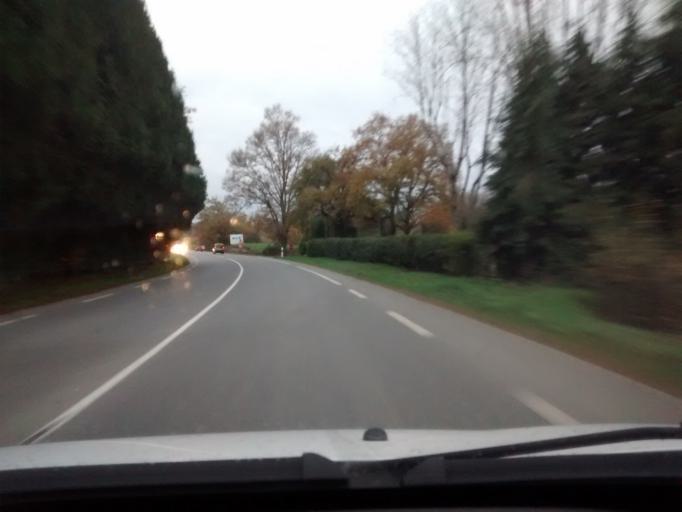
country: FR
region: Brittany
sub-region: Departement d'Ille-et-Vilaine
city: Fouillard
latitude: 48.1410
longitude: -1.5682
